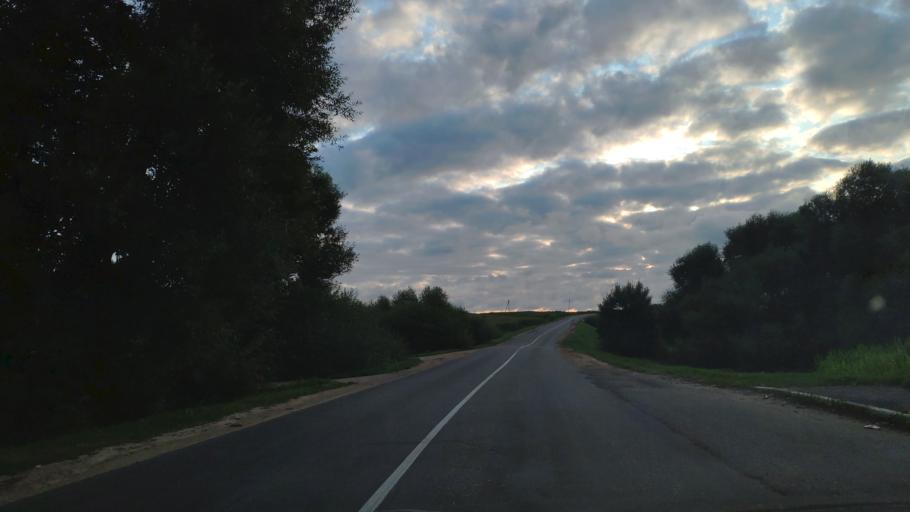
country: BY
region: Minsk
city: Azyartso
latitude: 53.8355
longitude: 27.3519
